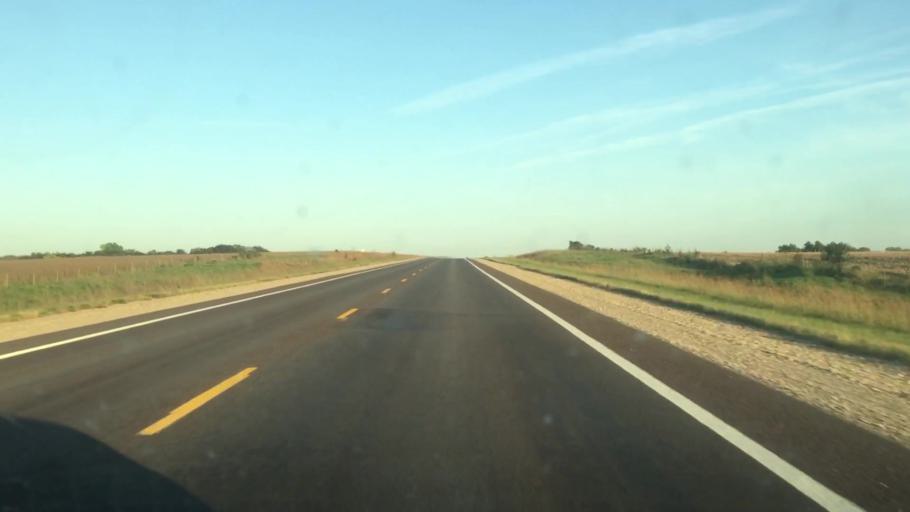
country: US
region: Kansas
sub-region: Atchison County
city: Atchison
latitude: 39.4308
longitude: -95.0804
